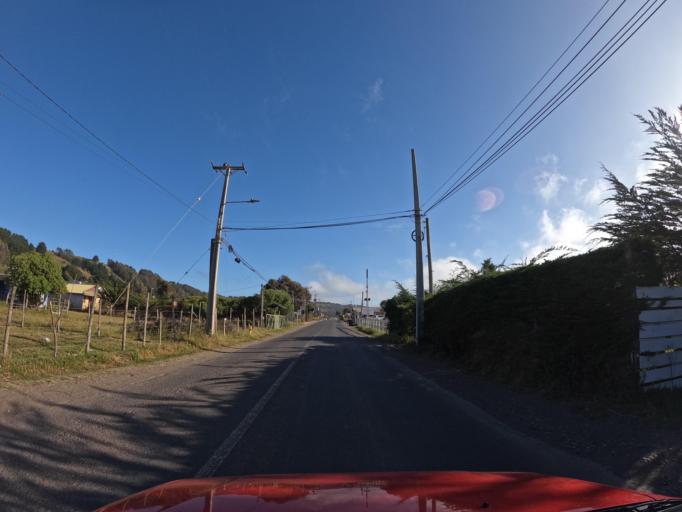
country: CL
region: Maule
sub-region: Provincia de Talca
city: Constitucion
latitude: -34.9266
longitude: -72.1794
